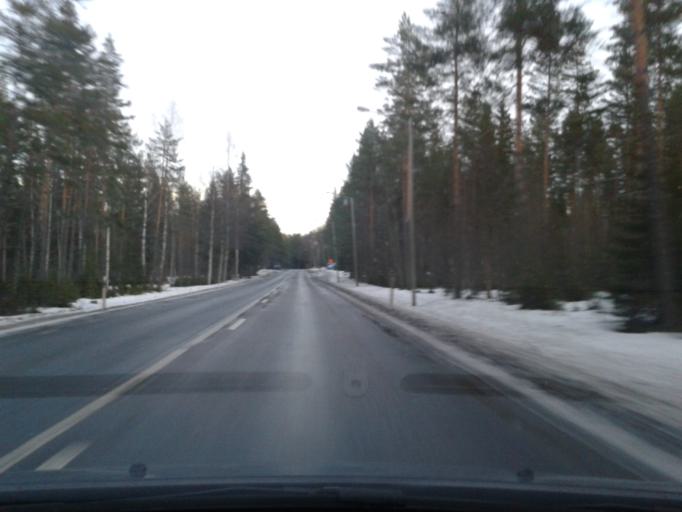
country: SE
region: Vaesternorrland
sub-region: Solleftea Kommun
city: Solleftea
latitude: 63.1486
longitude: 17.3453
